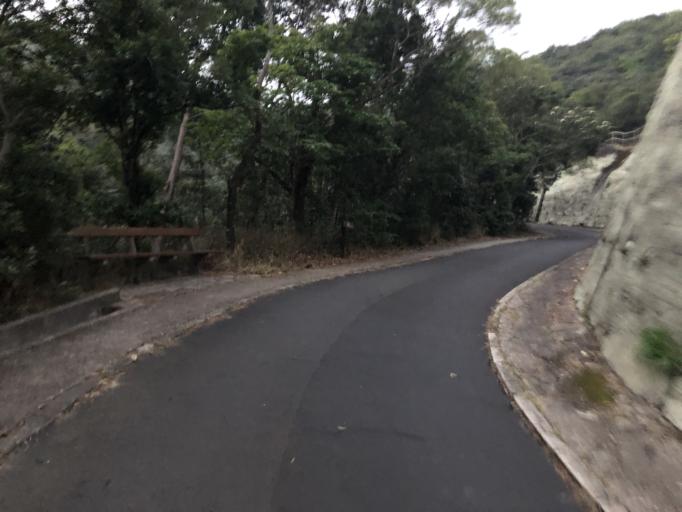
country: HK
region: Wanchai
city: Wan Chai
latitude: 22.2576
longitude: 114.2072
